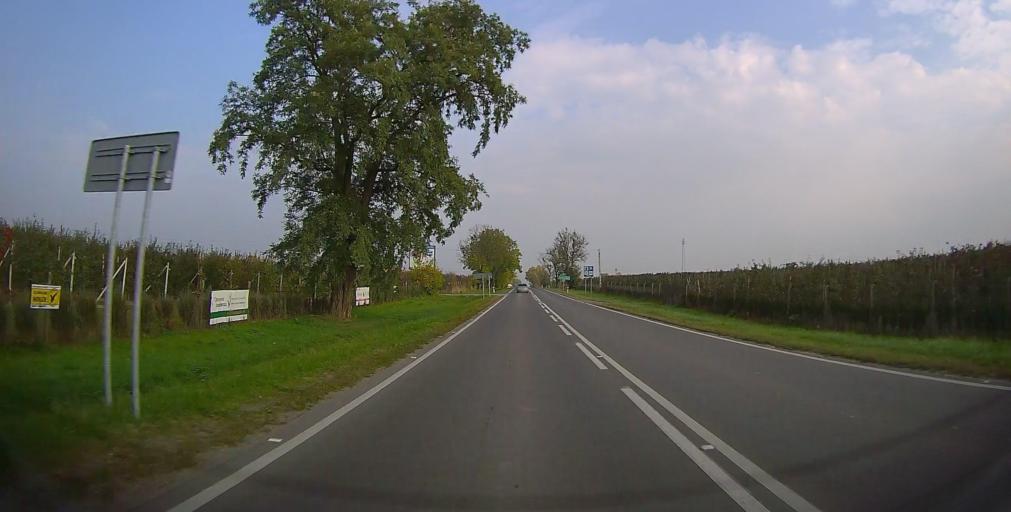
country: PL
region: Masovian Voivodeship
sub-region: Powiat grojecki
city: Mogielnica
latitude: 51.7318
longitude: 20.7526
